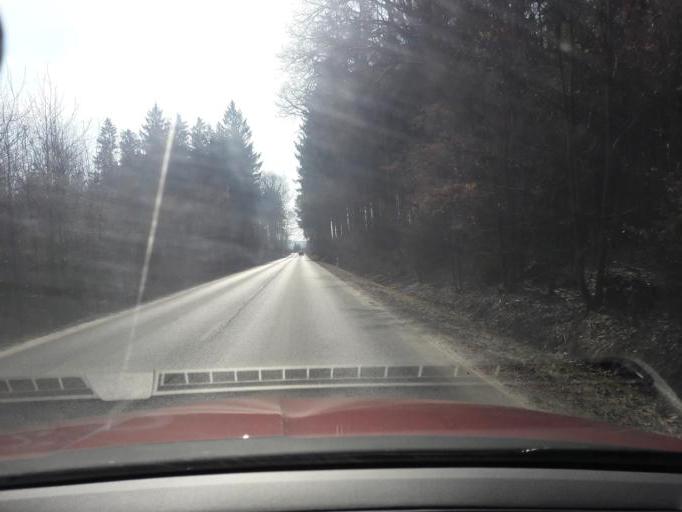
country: CZ
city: Novy Bor
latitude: 50.7517
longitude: 14.5673
